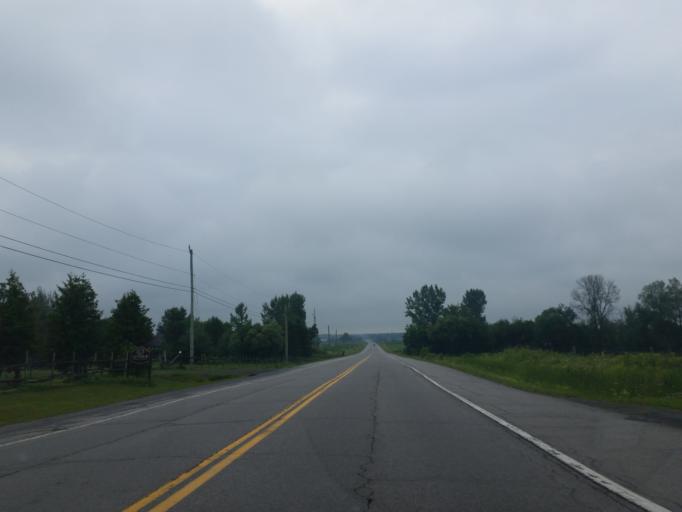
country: CA
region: Ontario
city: Clarence-Rockland
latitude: 45.4145
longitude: -75.4041
